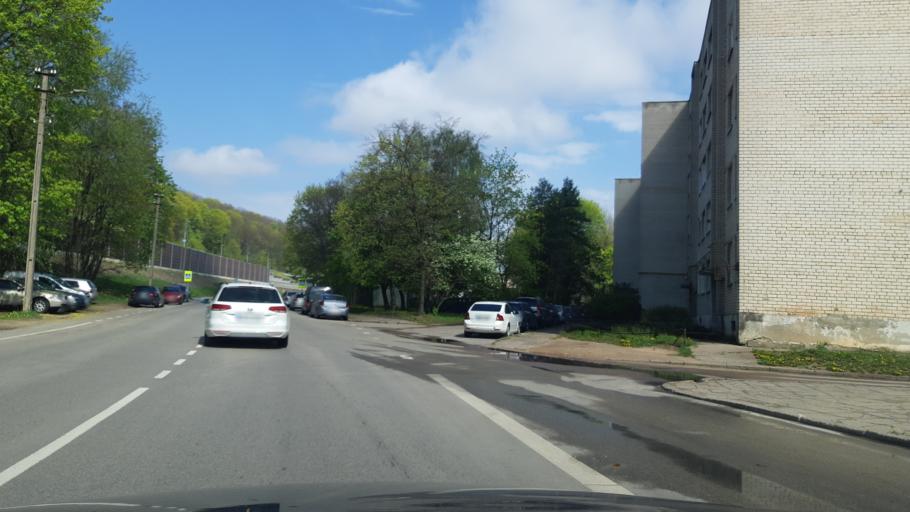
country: LT
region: Kauno apskritis
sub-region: Kaunas
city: Aleksotas
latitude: 54.8743
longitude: 23.9244
